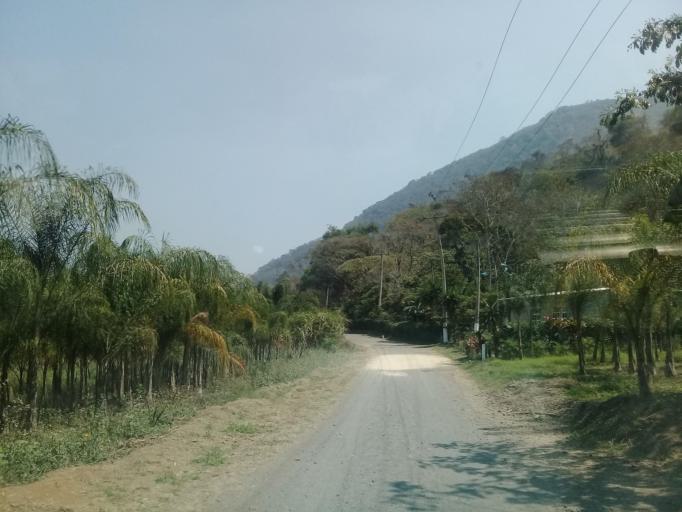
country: MX
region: Veracruz
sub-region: Ixtaczoquitlan
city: Capoluca
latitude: 18.8016
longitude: -96.9902
